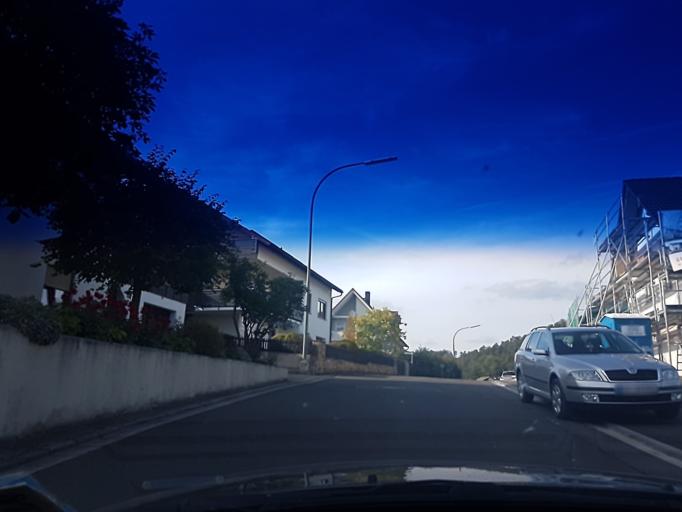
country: DE
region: Bavaria
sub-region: Regierungsbezirk Mittelfranken
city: Burghaslach
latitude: 49.7753
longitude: 10.5578
